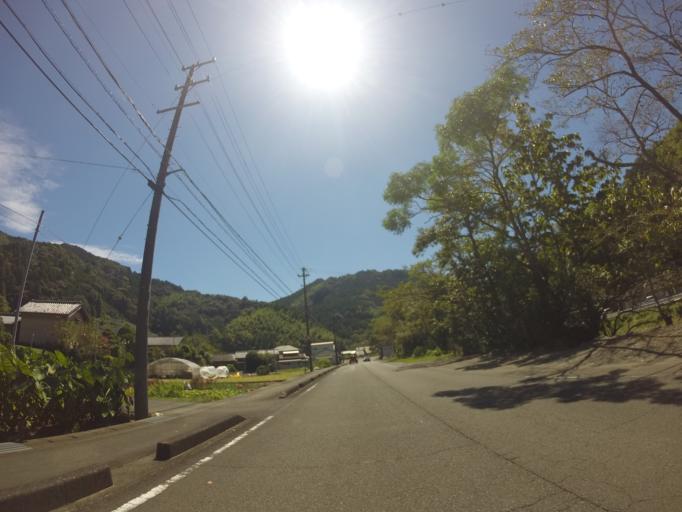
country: JP
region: Shizuoka
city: Fujieda
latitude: 34.9410
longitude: 138.2102
